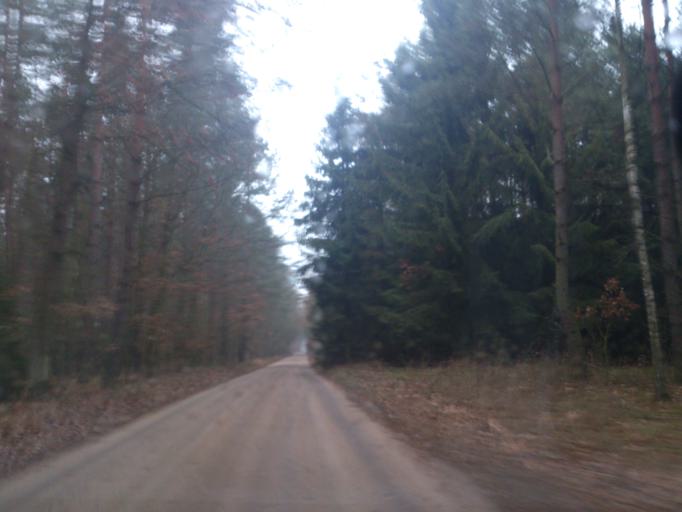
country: PL
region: Kujawsko-Pomorskie
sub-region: Powiat golubsko-dobrzynski
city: Radomin
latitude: 53.1471
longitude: 19.1394
